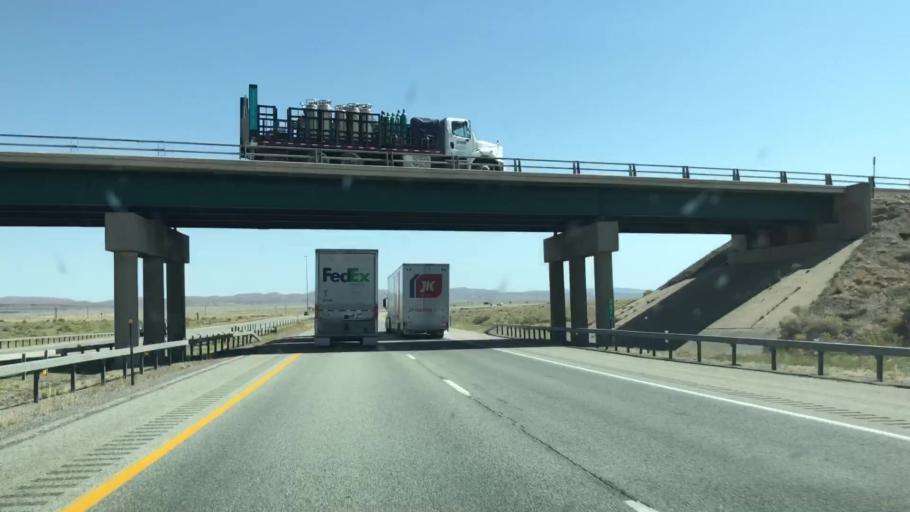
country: US
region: Wyoming
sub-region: Carbon County
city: Rawlins
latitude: 41.7721
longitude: -107.0779
